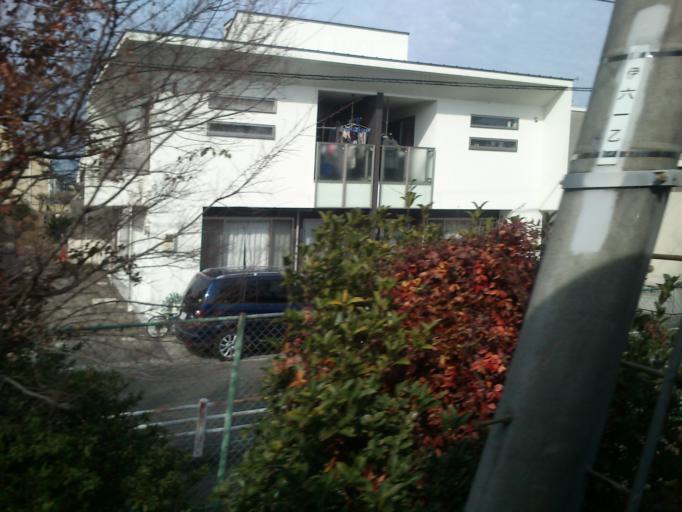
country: JP
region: Hyogo
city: Itami
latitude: 34.7735
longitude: 135.4155
